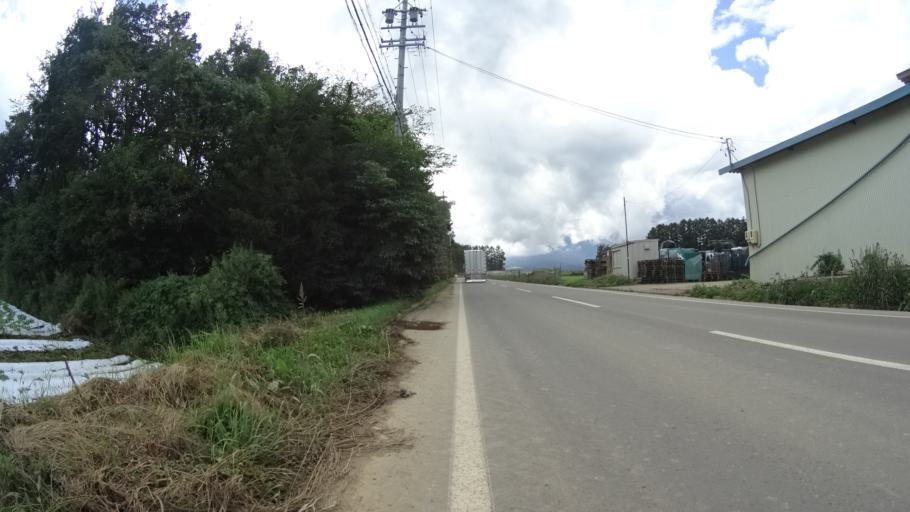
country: JP
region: Nagano
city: Saku
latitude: 35.9672
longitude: 138.5205
